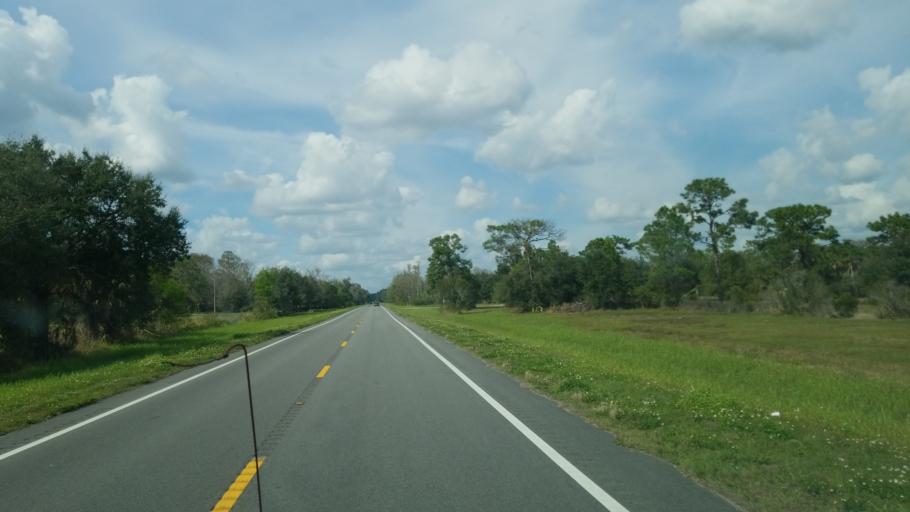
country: US
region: Florida
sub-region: Indian River County
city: Fellsmere
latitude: 27.7811
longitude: -80.9258
